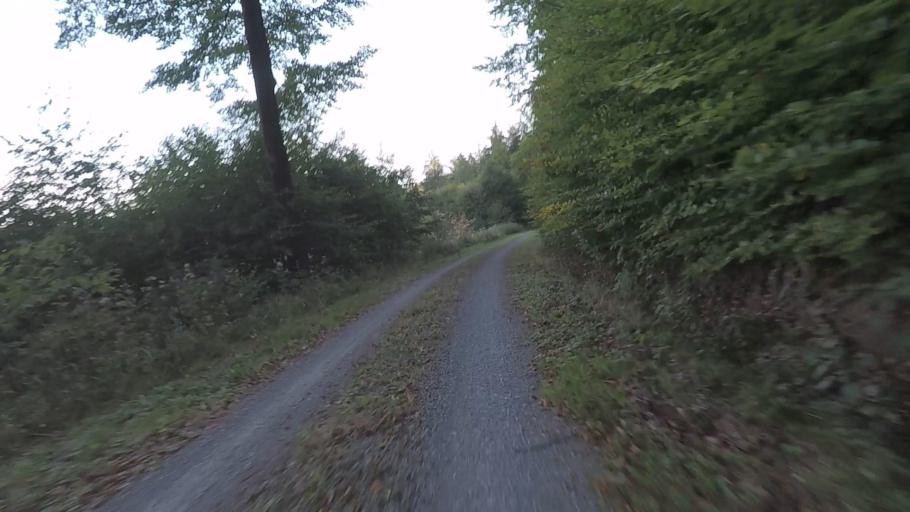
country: DE
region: Baden-Wuerttemberg
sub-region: Regierungsbezirk Stuttgart
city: Spiegelberg
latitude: 49.0494
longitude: 9.4538
